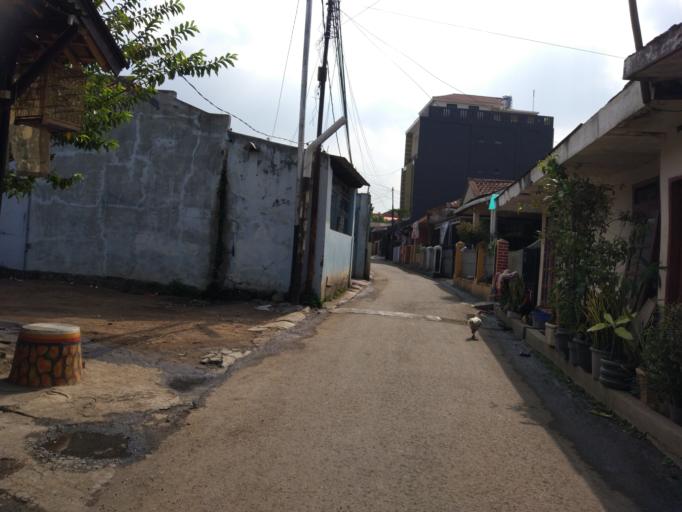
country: ID
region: West Java
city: Cileunyi
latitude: -6.9092
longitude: 107.6922
